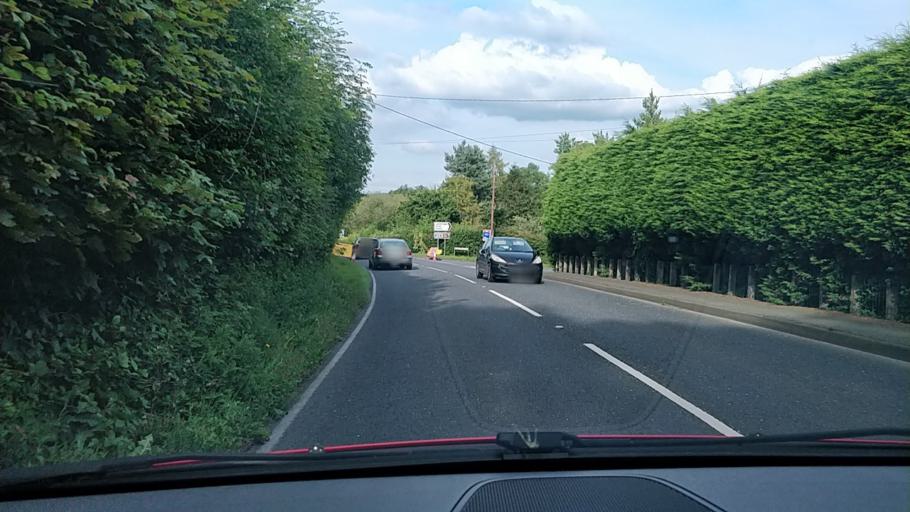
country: GB
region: Wales
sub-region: County of Flintshire
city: Leeswood
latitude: 53.1142
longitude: -3.1072
